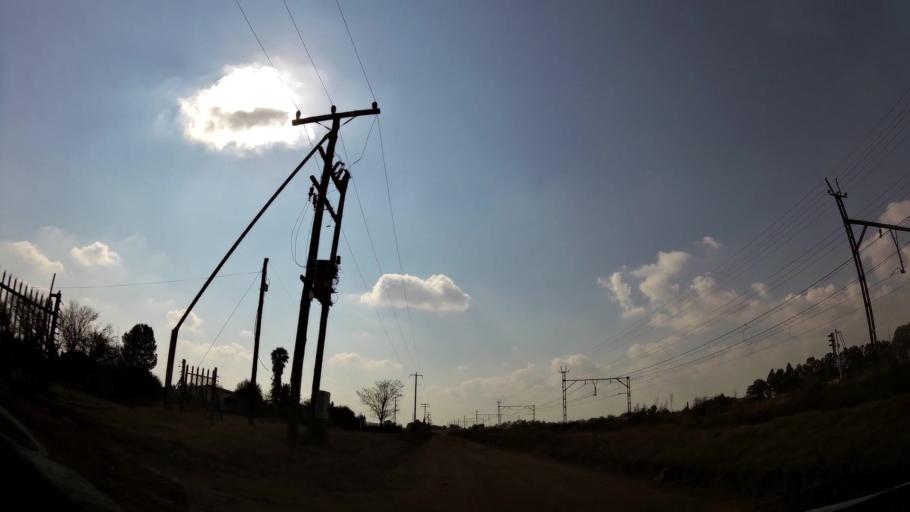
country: ZA
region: Gauteng
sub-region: Ekurhuleni Metropolitan Municipality
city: Springs
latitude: -26.1953
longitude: 28.5354
